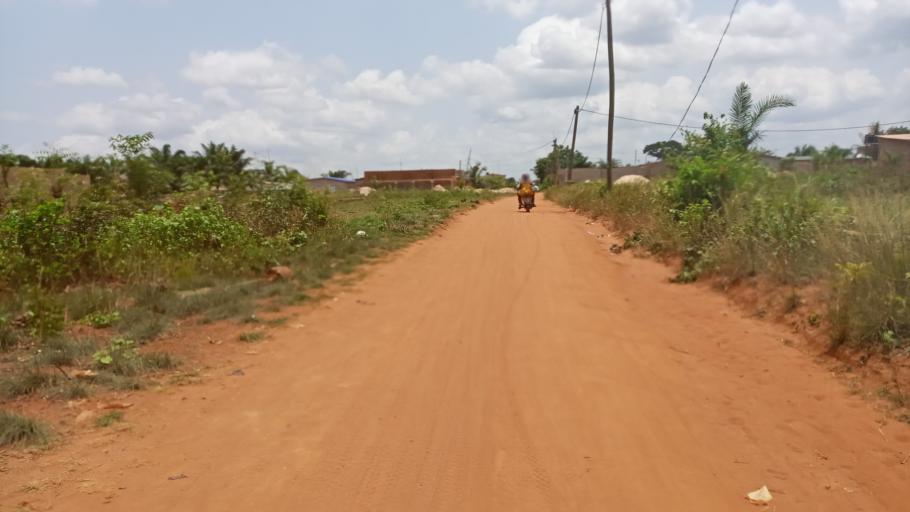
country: TG
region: Maritime
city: Tsevie
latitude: 6.2934
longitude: 1.1353
